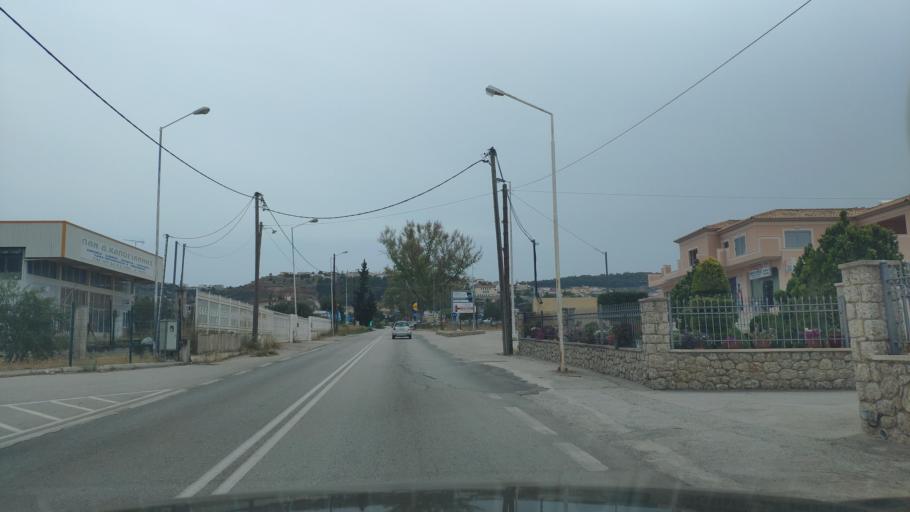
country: GR
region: Peloponnese
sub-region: Nomos Argolidos
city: Kranidi
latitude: 37.3915
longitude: 23.1576
